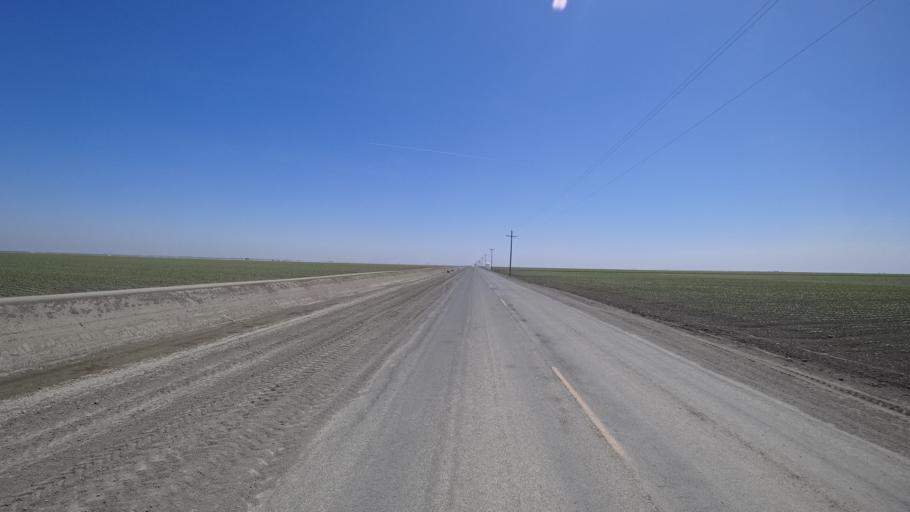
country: US
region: California
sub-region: Kings County
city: Corcoran
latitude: 36.0213
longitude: -119.6811
